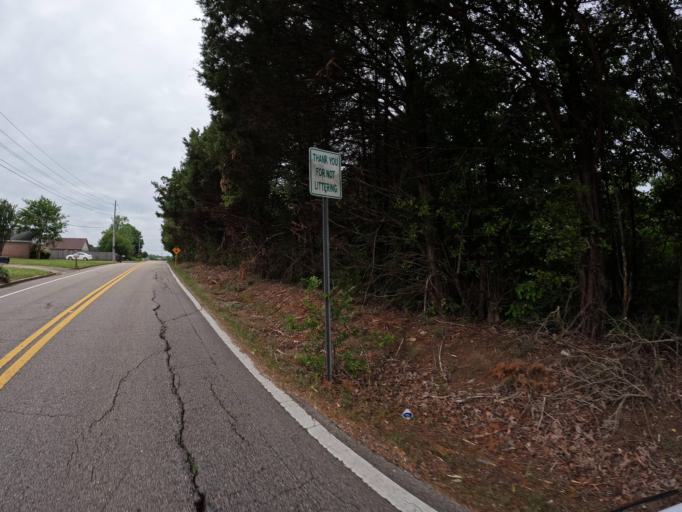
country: US
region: Mississippi
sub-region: Lee County
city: Tupelo
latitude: 34.2834
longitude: -88.7652
